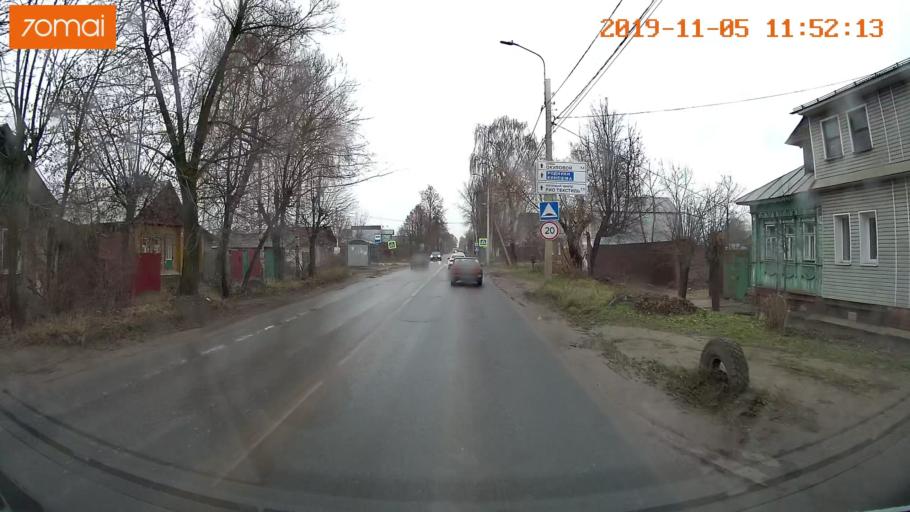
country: RU
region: Ivanovo
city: Bogorodskoye
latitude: 57.0010
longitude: 41.0292
